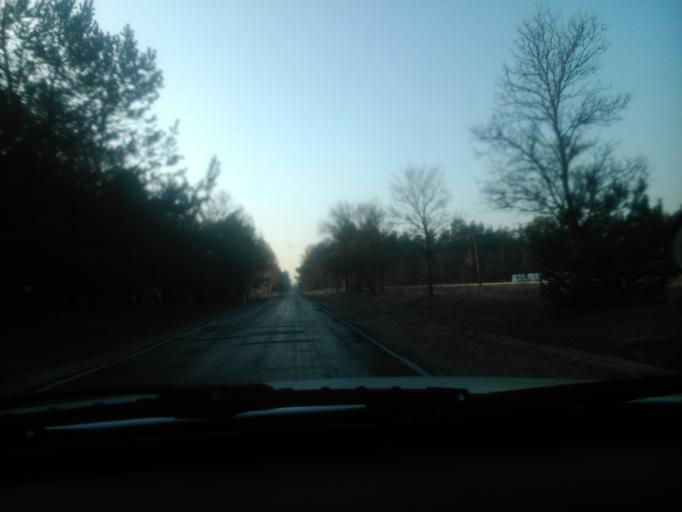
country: PL
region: Masovian Voivodeship
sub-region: Powiat ostrolecki
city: Czarnia
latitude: 53.3024
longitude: 21.0621
